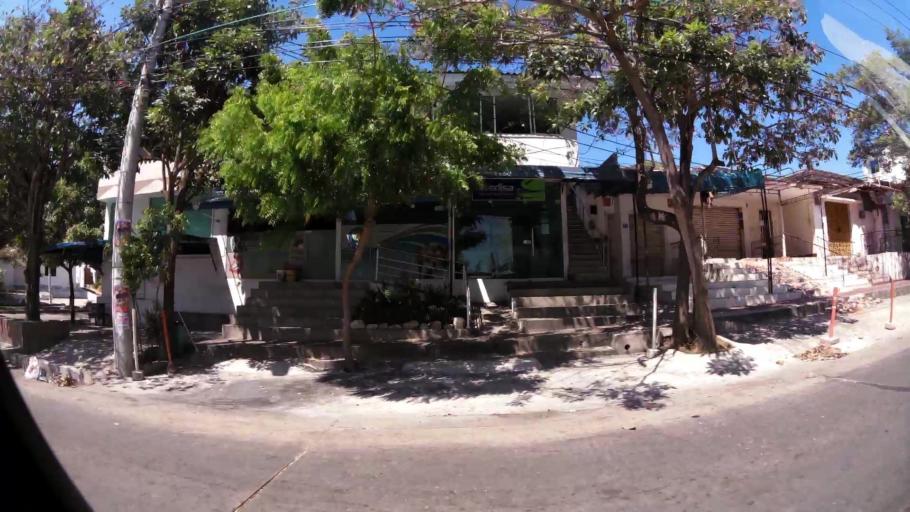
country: CO
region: Atlantico
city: Barranquilla
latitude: 10.9994
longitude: -74.8142
